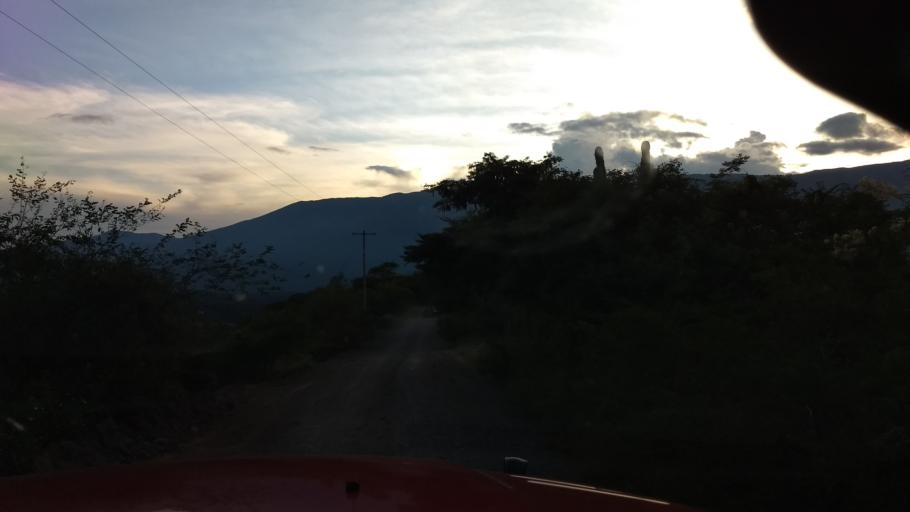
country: MX
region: Colima
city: Suchitlan
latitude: 19.4823
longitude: -103.7979
